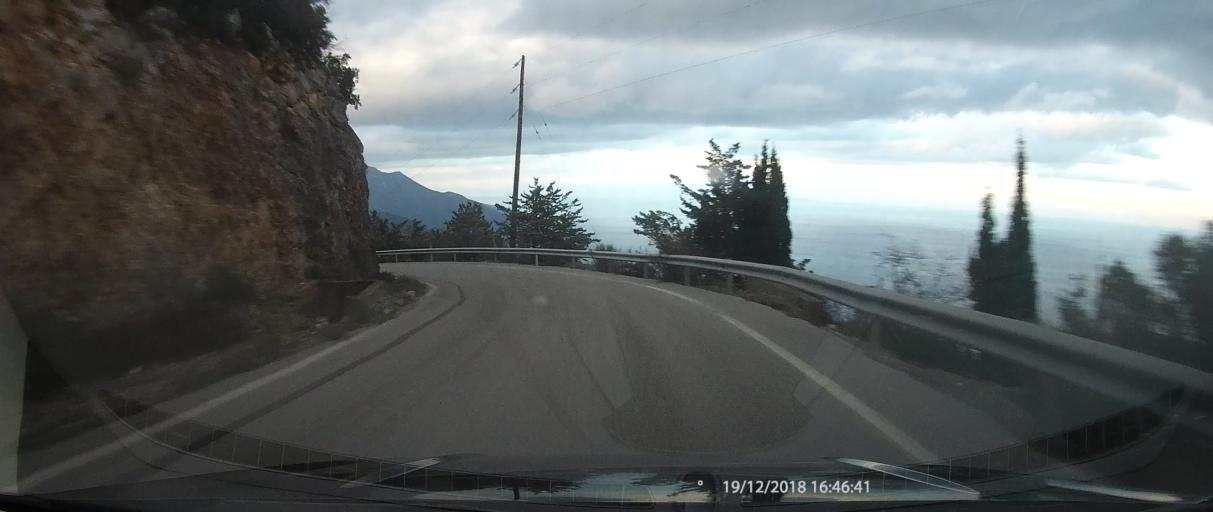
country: GR
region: Peloponnese
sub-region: Nomos Lakonias
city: Sykea
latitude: 36.9244
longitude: 23.0084
